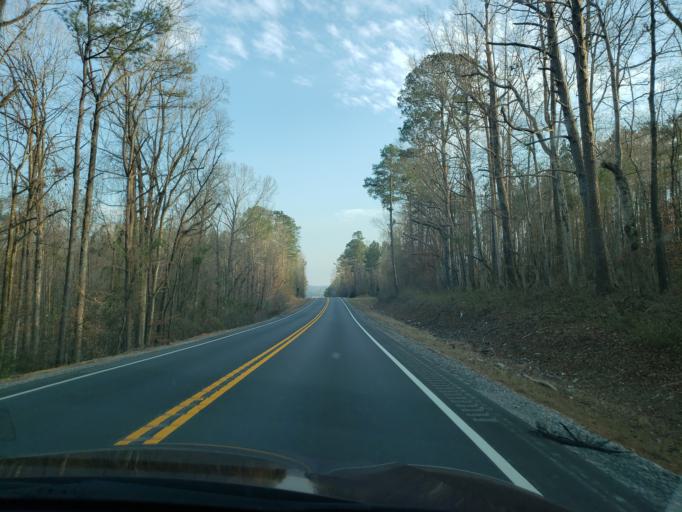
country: US
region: Alabama
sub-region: Hale County
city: Greensboro
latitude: 32.8397
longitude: -87.6083
